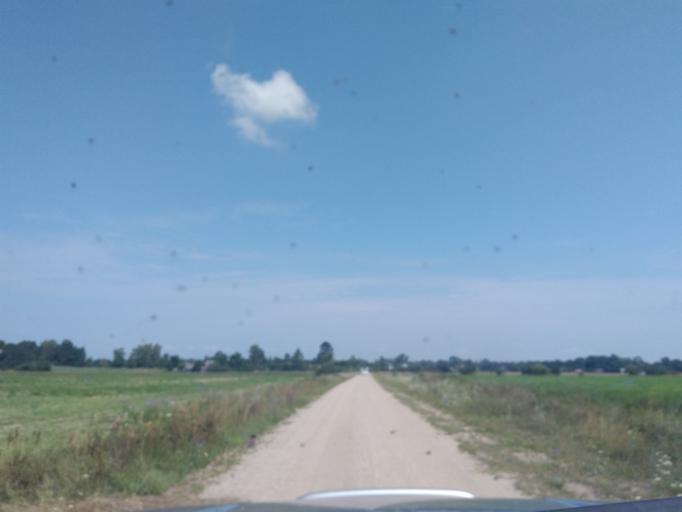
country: BY
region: Minsk
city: Valozhyn
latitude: 54.0046
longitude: 26.5711
